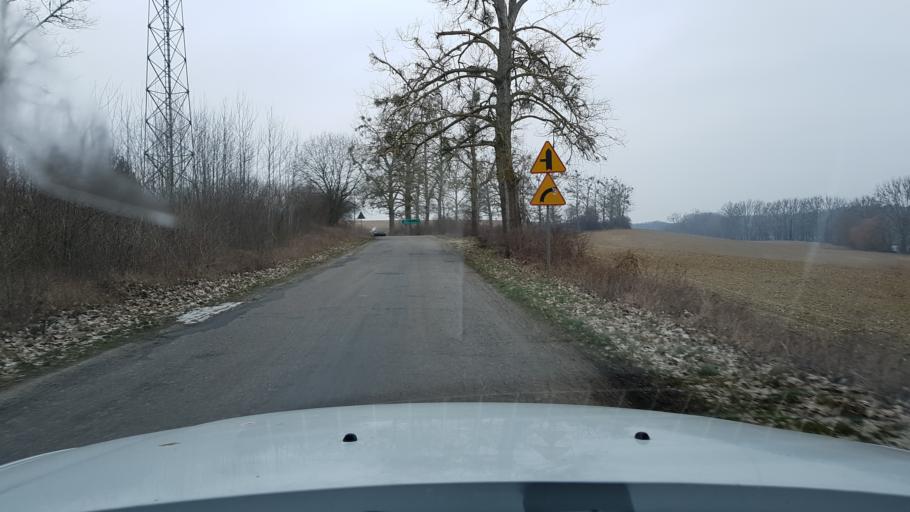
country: PL
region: West Pomeranian Voivodeship
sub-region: Powiat gryfinski
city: Gryfino
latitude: 53.2150
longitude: 14.5992
